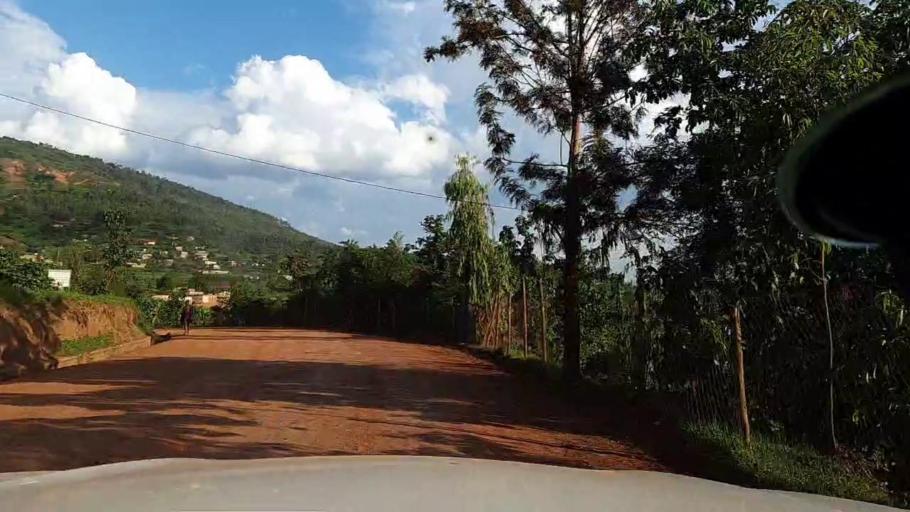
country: RW
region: Kigali
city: Kigali
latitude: -1.9149
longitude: 29.9865
